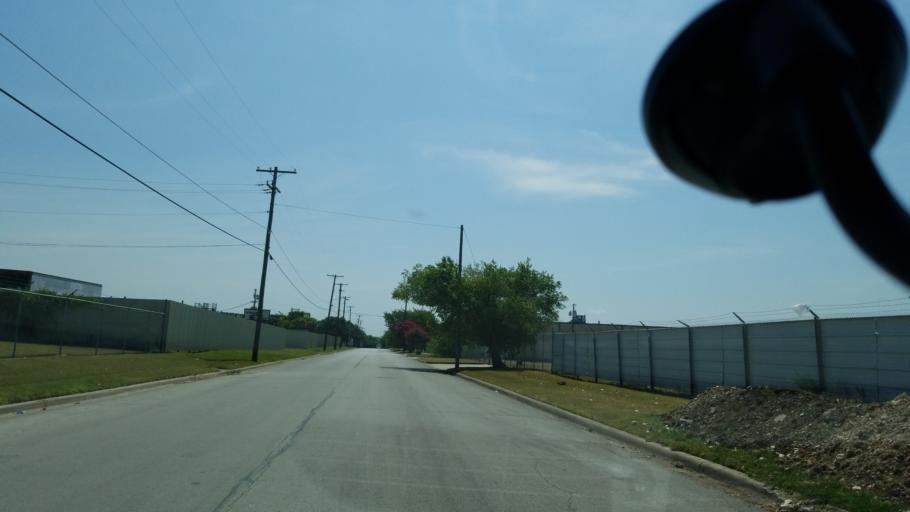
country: US
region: Texas
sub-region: Dallas County
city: Cockrell Hill
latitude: 32.7155
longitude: -96.8715
